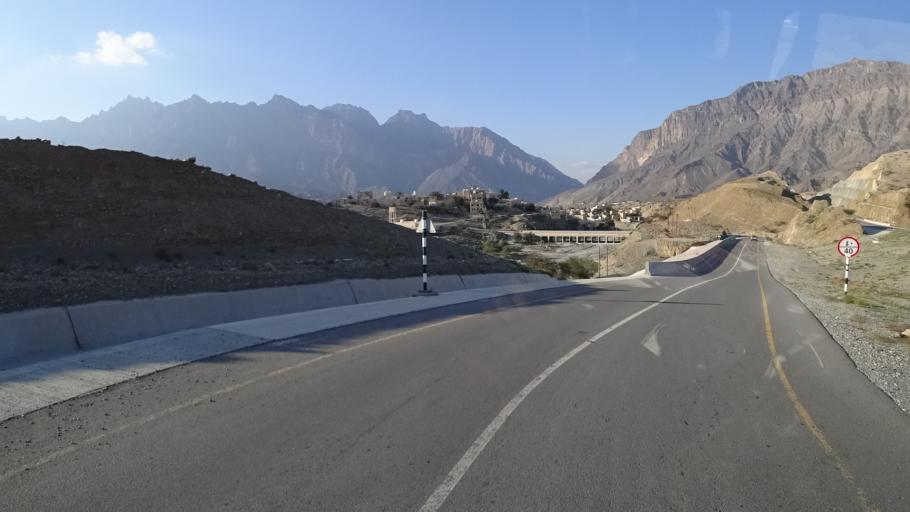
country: OM
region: Al Batinah
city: Rustaq
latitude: 23.2828
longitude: 57.3337
